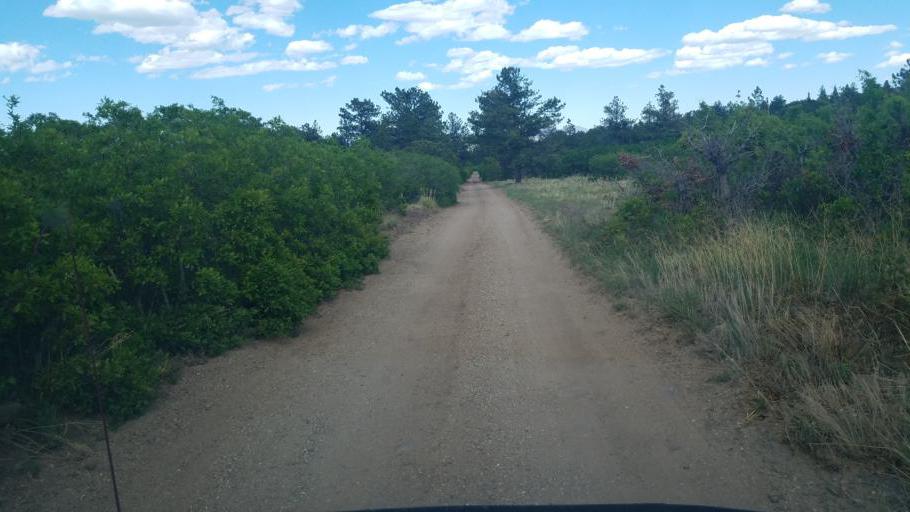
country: US
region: Colorado
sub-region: Custer County
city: Westcliffe
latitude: 38.2218
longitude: -105.6095
